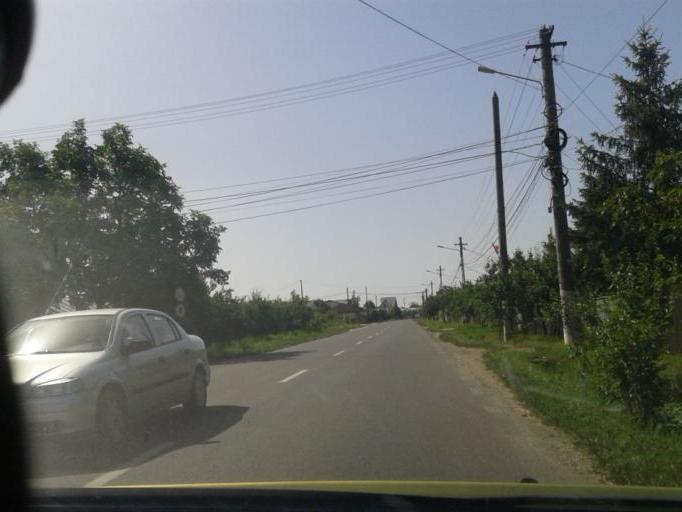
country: RO
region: Prahova
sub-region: Comuna Paulesti
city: Gageni
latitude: 45.0324
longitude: 25.9419
